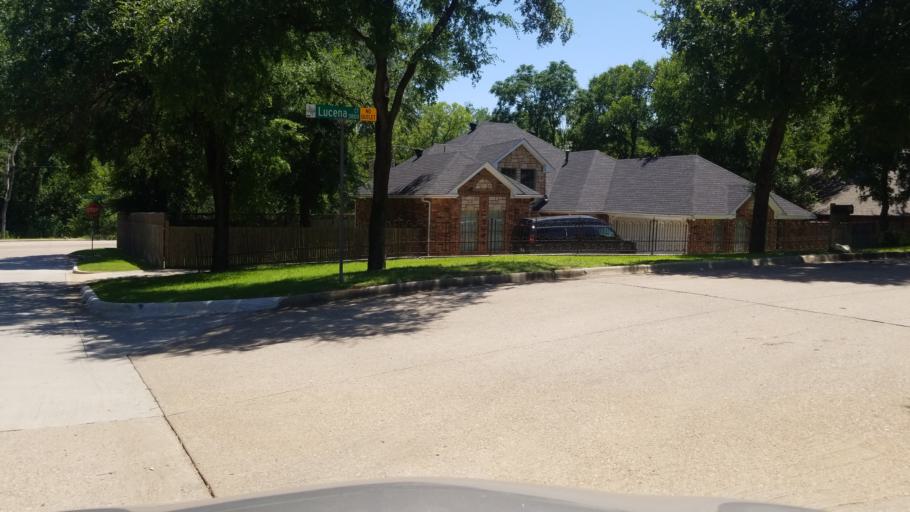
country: US
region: Texas
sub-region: Dallas County
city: Grand Prairie
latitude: 32.6793
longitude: -97.0007
